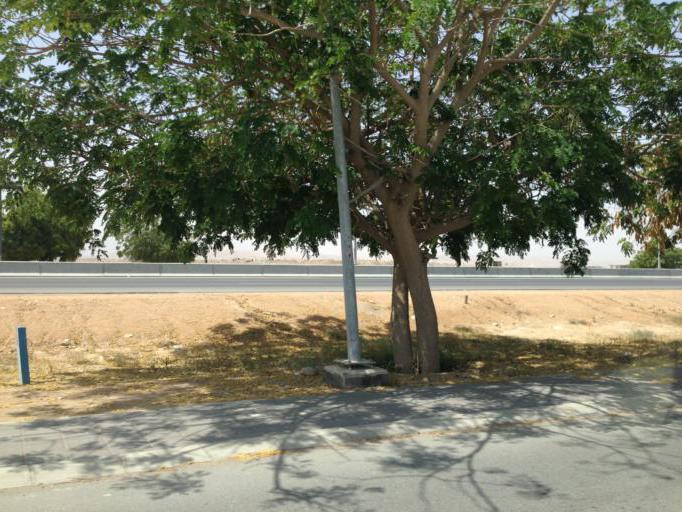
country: OM
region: Muhafazat Masqat
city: Bawshar
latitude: 23.6038
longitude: 58.3376
